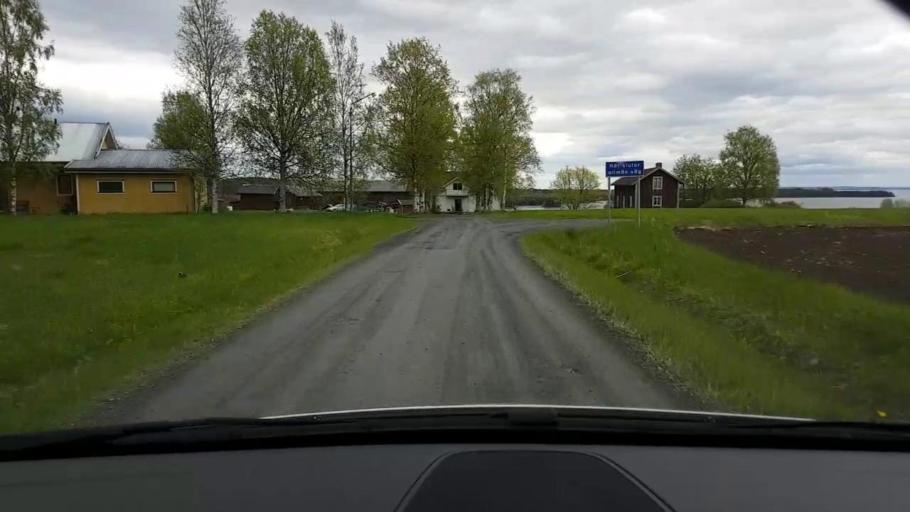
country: SE
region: Jaemtland
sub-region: Krokoms Kommun
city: Valla
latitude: 63.3026
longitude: 14.0419
